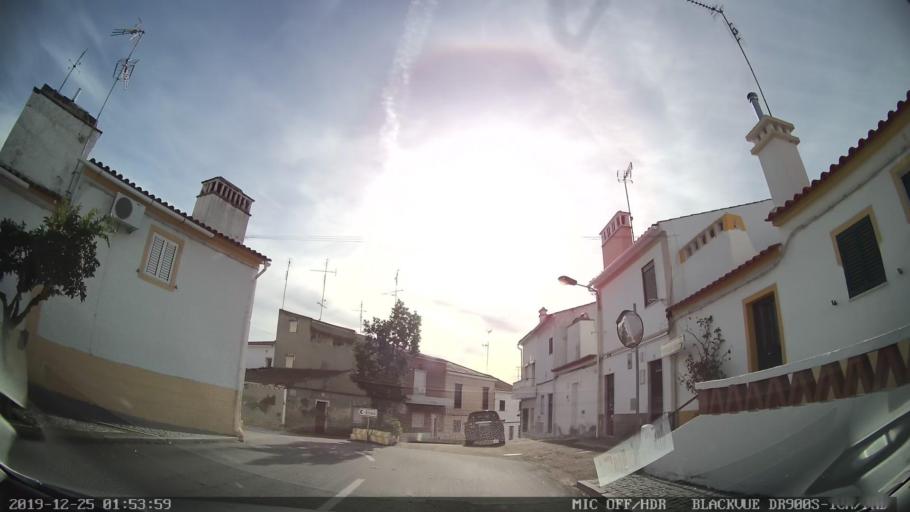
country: PT
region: Portalegre
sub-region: Arronches
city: Arronches
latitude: 39.0060
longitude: -7.2503
